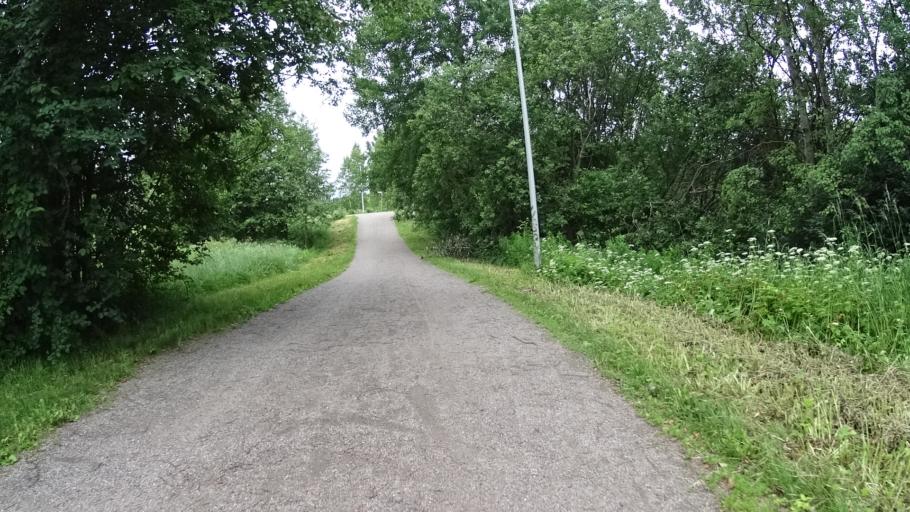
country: FI
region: Uusimaa
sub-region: Helsinki
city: Teekkarikylae
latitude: 60.2722
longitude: 24.8798
